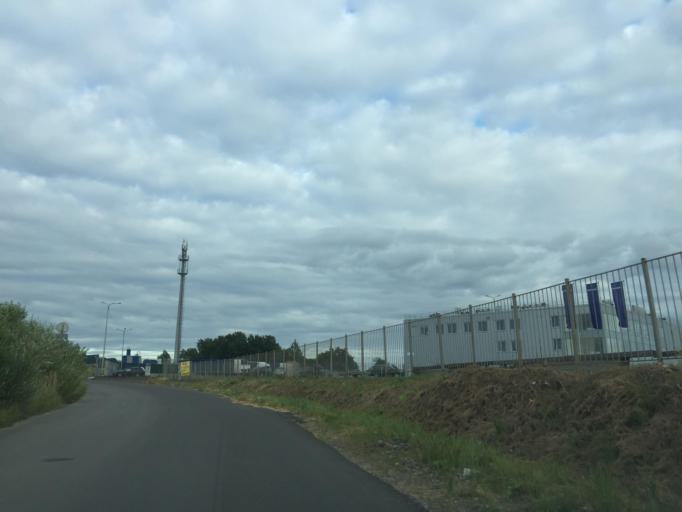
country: RU
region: Leningrad
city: Bugry
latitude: 60.0851
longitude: 30.3804
